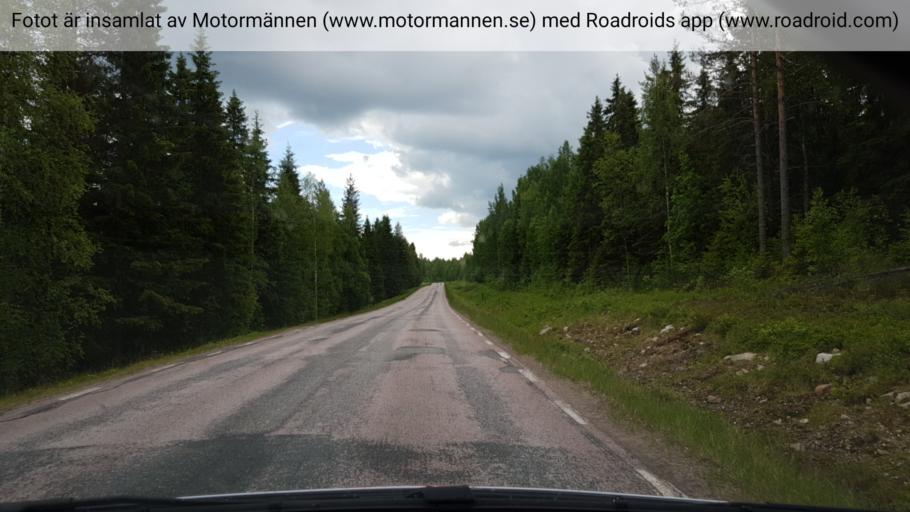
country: FI
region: Lapland
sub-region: Torniolaakso
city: Ylitornio
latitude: 66.2055
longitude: 23.6999
